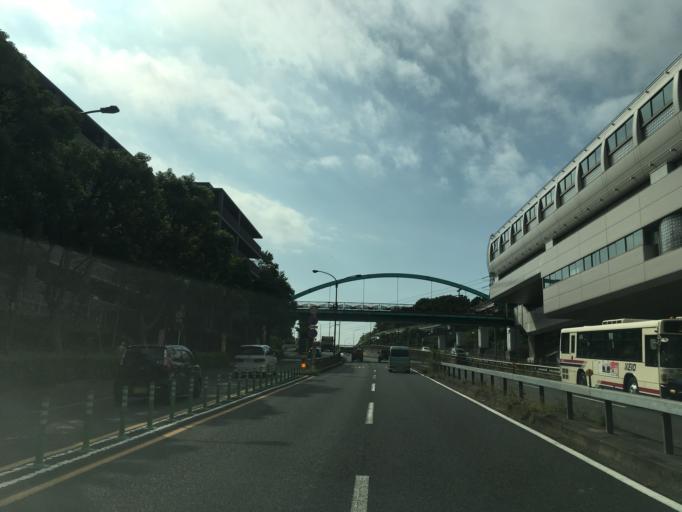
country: JP
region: Tokyo
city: Hino
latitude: 35.6322
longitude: 139.4223
